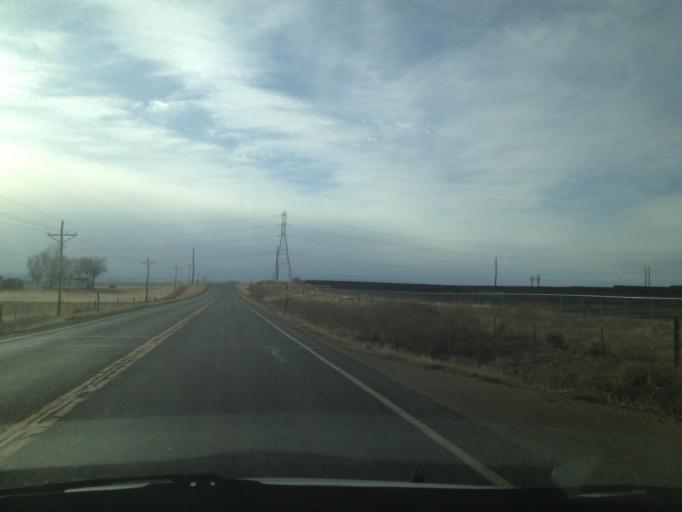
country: US
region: Colorado
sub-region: Weld County
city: Aristocrat Ranchettes
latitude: 40.0804
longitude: -104.7491
